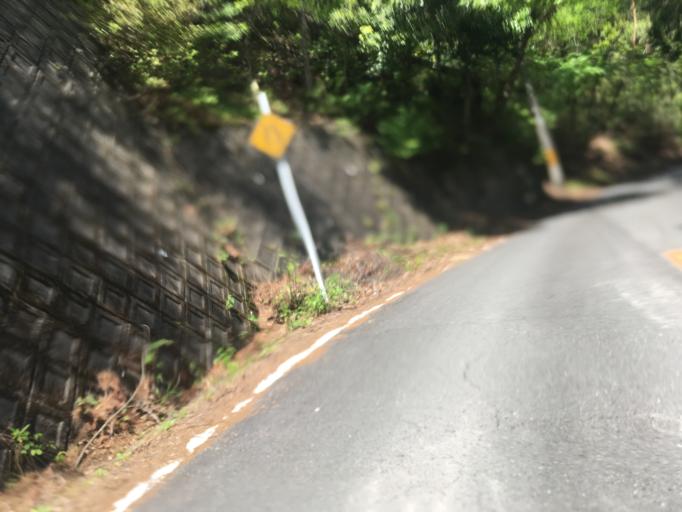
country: JP
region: Kyoto
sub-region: Kyoto-shi
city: Kamigyo-ku
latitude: 35.0648
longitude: 135.7225
